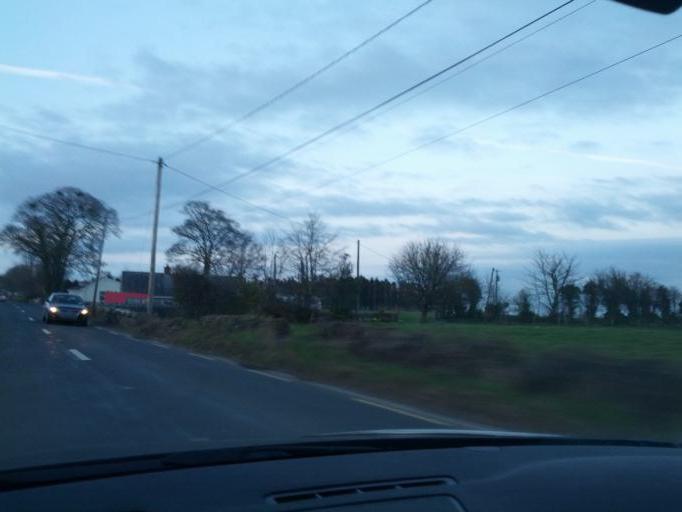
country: IE
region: Connaught
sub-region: County Galway
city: Portumna
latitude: 53.0240
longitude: -8.1238
